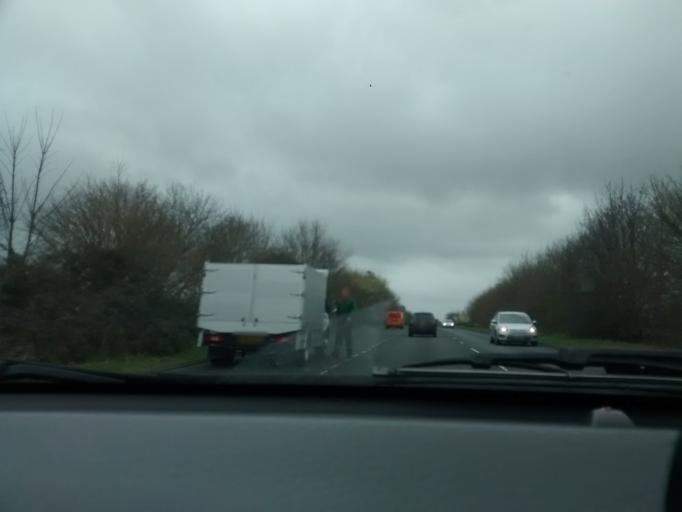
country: GB
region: England
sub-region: Suffolk
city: Felixstowe
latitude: 51.9740
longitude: 1.3428
